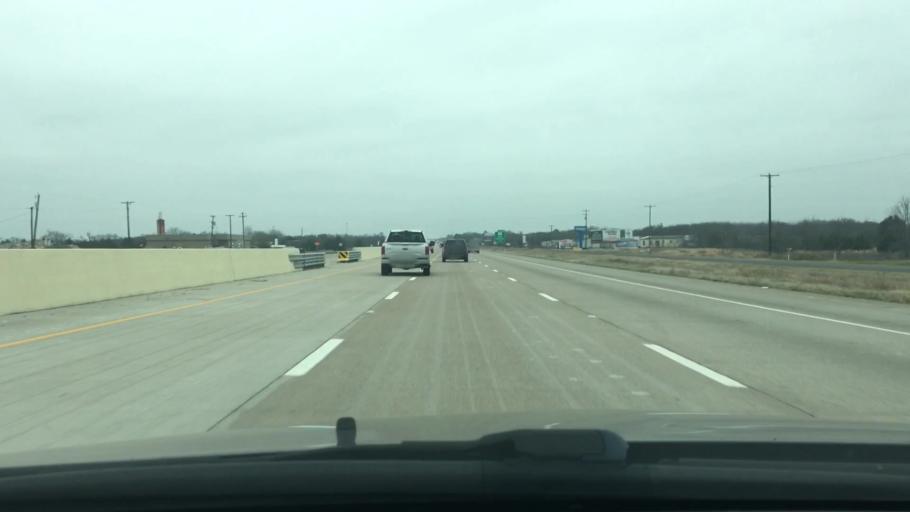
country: US
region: Texas
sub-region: Navarro County
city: Corsicana
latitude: 32.0273
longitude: -96.4416
